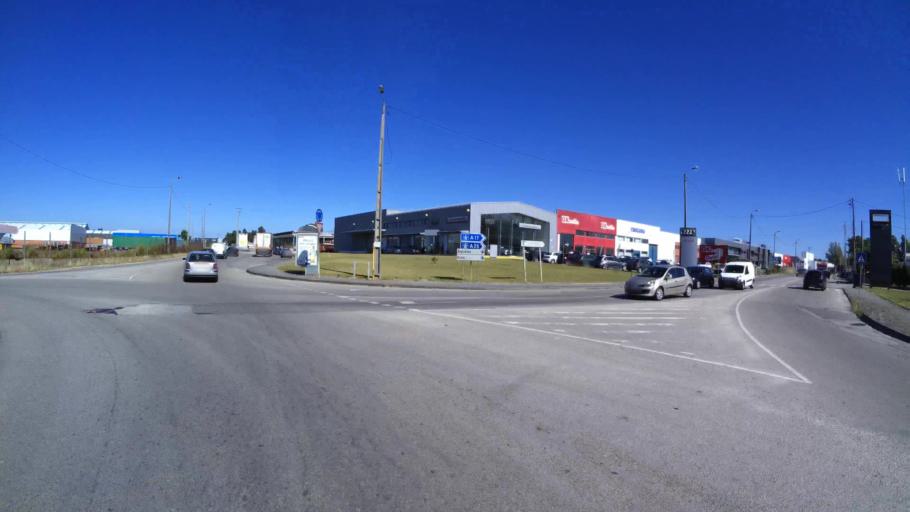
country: PT
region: Aveiro
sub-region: Aveiro
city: Aveiro
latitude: 40.6511
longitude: -8.6083
